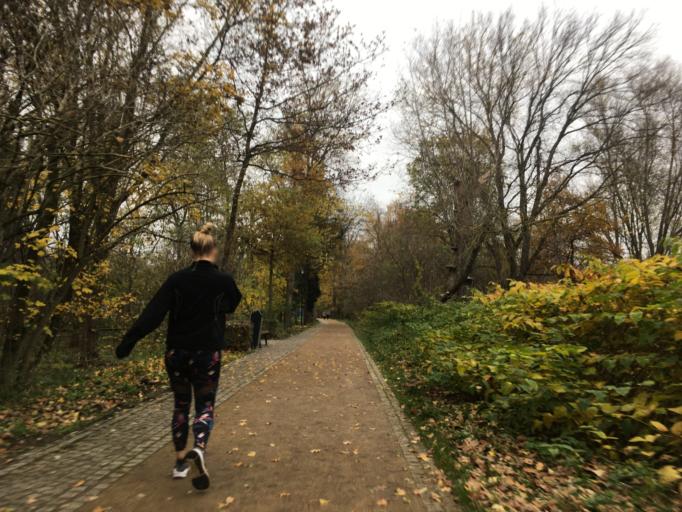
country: DE
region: Brandenburg
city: Frankfurt (Oder)
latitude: 52.3373
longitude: 14.5594
